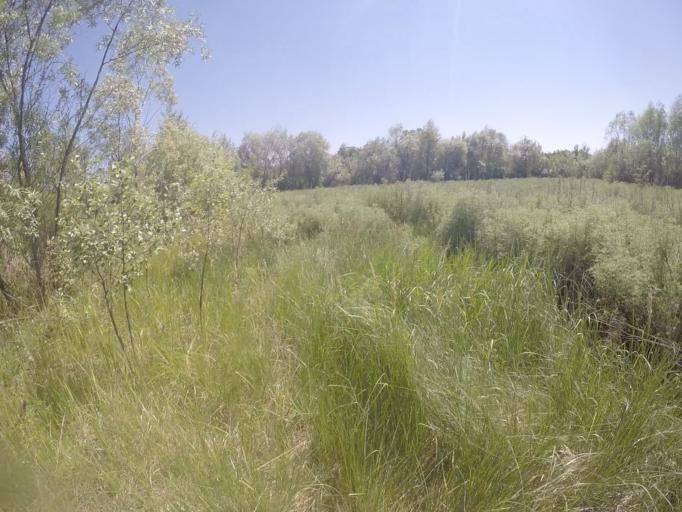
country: RU
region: Saratov
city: Krasnyy Oktyabr'
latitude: 51.3099
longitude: 45.5500
